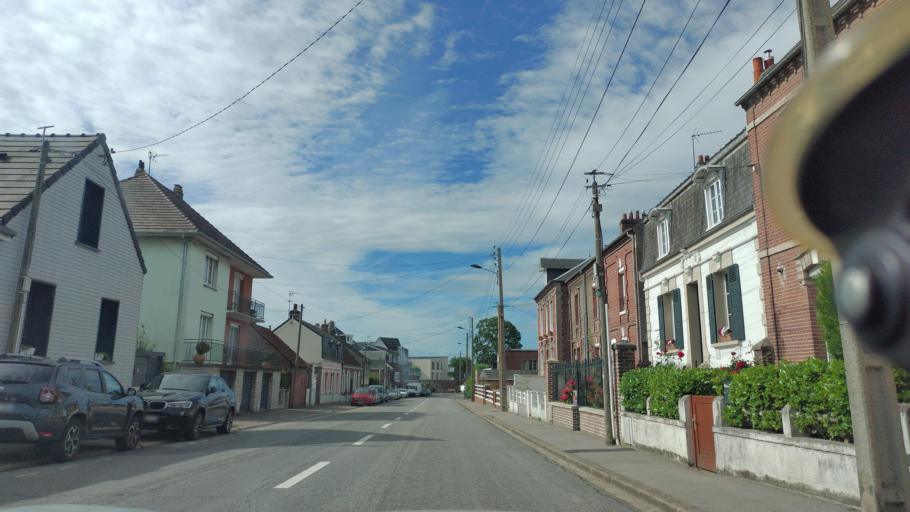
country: FR
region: Haute-Normandie
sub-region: Departement de la Seine-Maritime
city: Eu
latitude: 50.0575
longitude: 1.4245
